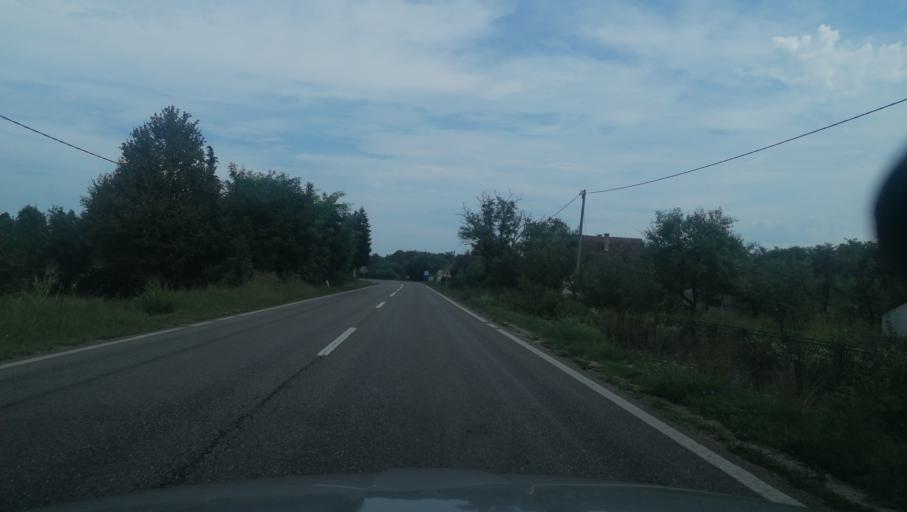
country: BA
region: Federation of Bosnia and Herzegovina
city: Odzak
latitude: 44.9702
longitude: 18.3479
